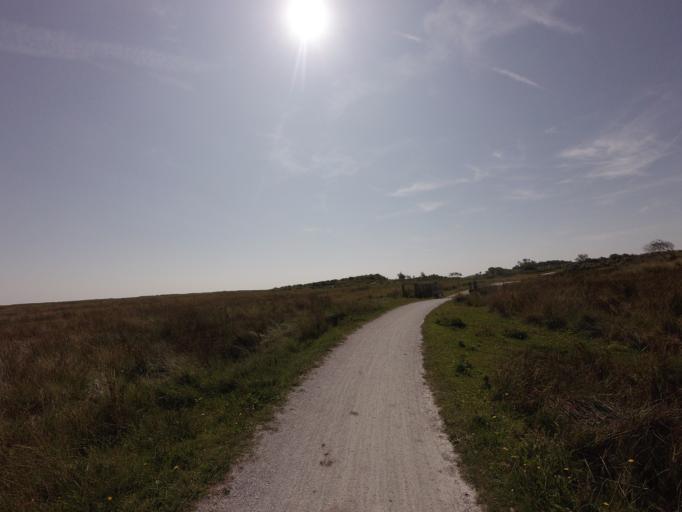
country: NL
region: Friesland
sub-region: Gemeente Schiermonnikoog
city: Schiermonnikoog
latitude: 53.4815
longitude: 6.2116
